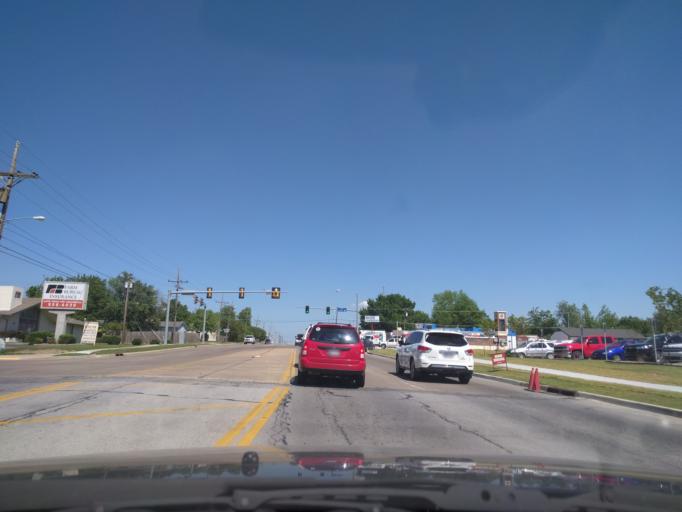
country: US
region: Oklahoma
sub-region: Tulsa County
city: Broken Arrow
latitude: 36.0609
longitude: -95.7917
